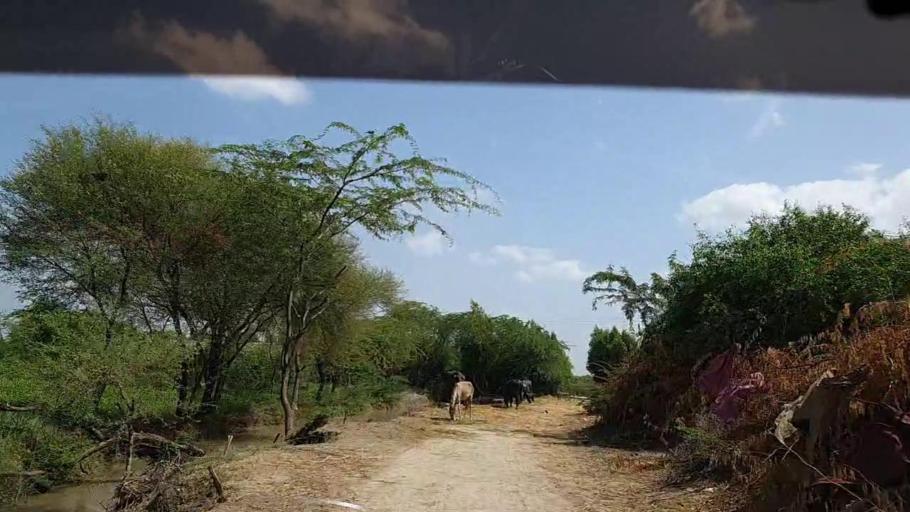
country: PK
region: Sindh
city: Badin
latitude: 24.5904
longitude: 68.8024
